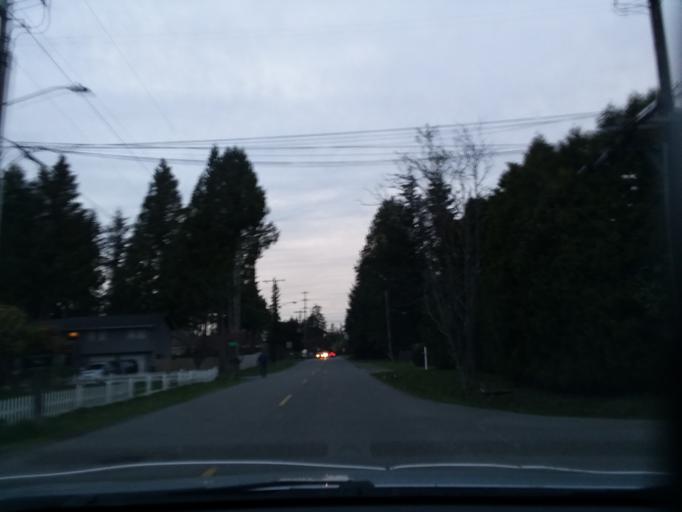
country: US
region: Washington
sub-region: Snohomish County
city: Esperance
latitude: 47.7978
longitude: -122.3518
